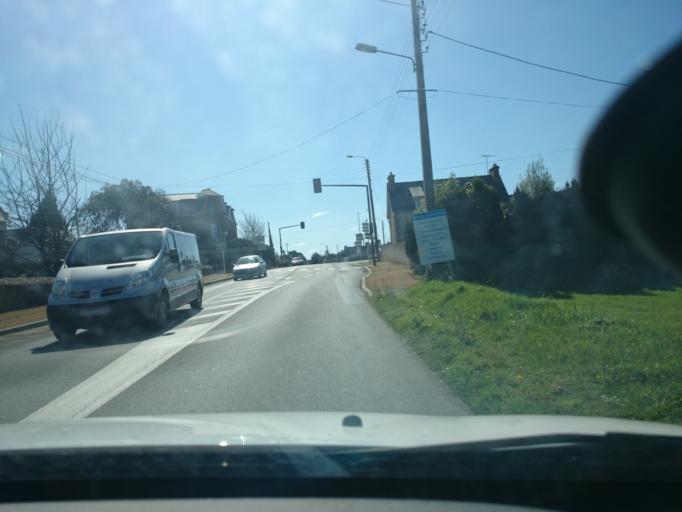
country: FR
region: Brittany
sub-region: Departement des Cotes-d'Armor
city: Tregastel
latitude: 48.8194
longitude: -3.4702
